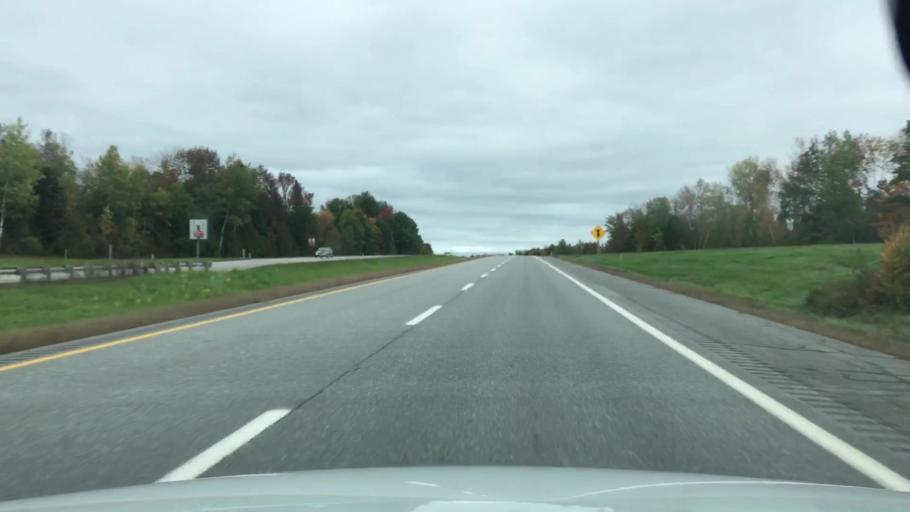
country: US
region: Maine
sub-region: Penobscot County
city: Newport
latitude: 44.8182
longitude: -69.2589
